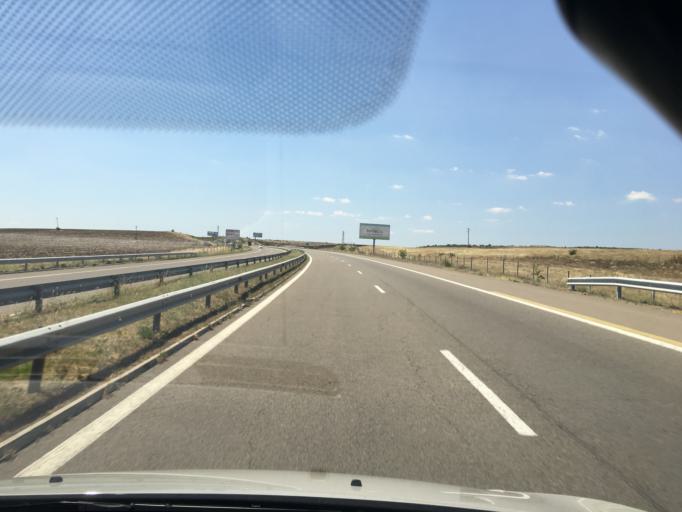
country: BG
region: Burgas
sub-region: Obshtina Kameno
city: Kameno
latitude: 42.5959
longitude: 27.1596
